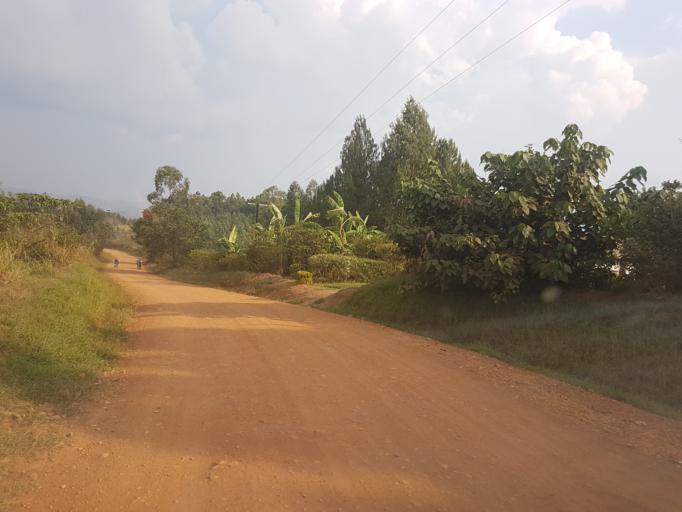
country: UG
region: Western Region
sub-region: Rukungiri District
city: Rukungiri
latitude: -0.6557
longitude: 29.8613
